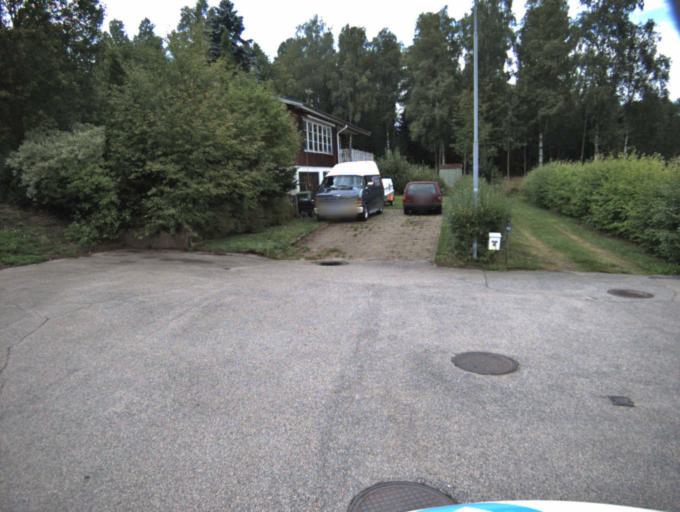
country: SE
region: Vaestra Goetaland
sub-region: Ulricehamns Kommun
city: Ulricehamn
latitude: 57.8619
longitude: 13.4191
